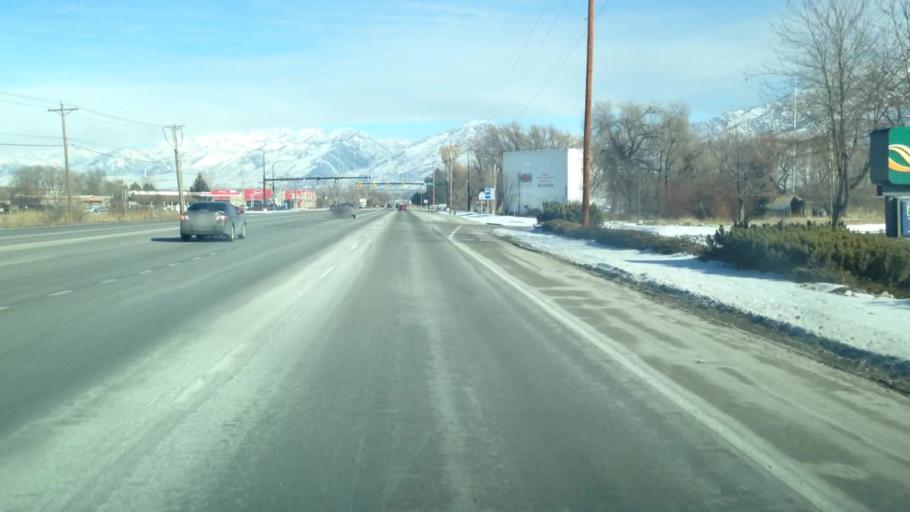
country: US
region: Utah
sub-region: Cache County
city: Nibley
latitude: 41.6960
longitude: -111.8616
